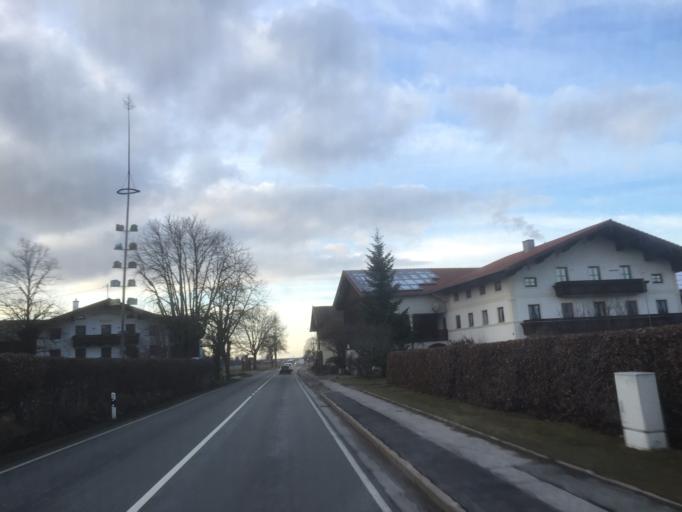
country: DE
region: Bavaria
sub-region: Upper Bavaria
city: Nussdorf
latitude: 47.8867
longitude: 12.5769
